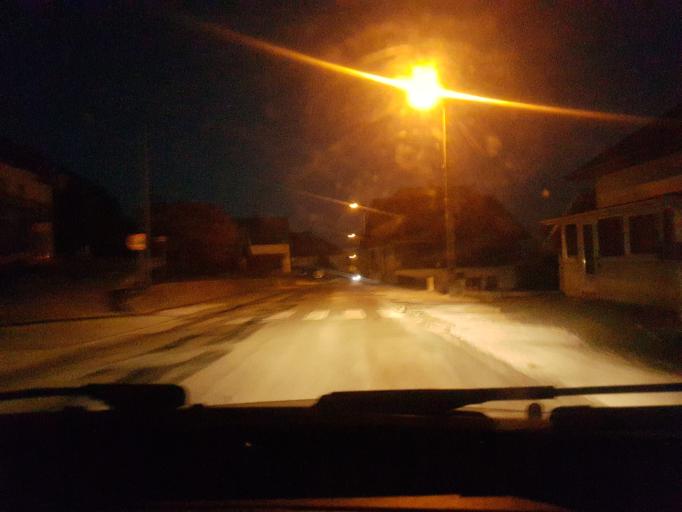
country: FR
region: Franche-Comte
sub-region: Departement du Doubs
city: Le Russey
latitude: 47.1995
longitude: 6.7429
